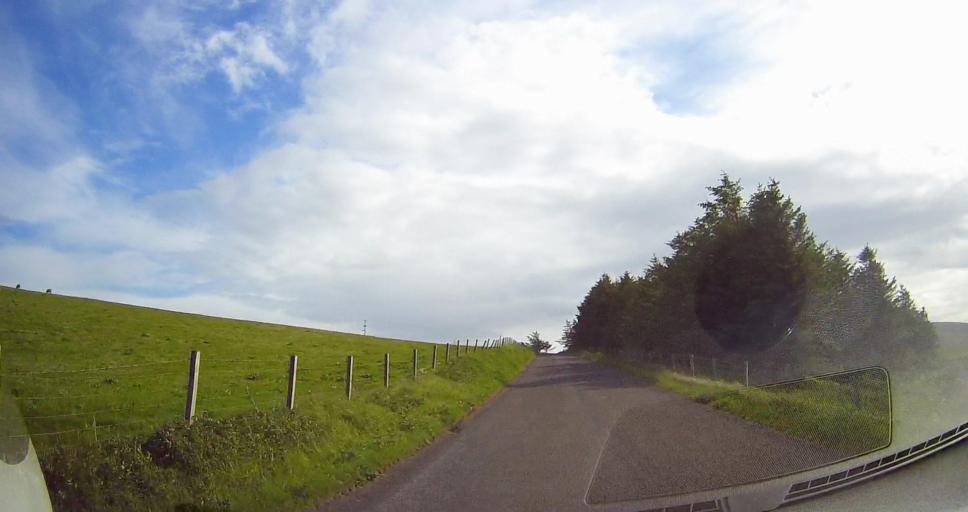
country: GB
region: Scotland
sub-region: Orkney Islands
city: Stromness
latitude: 58.8257
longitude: -3.2092
